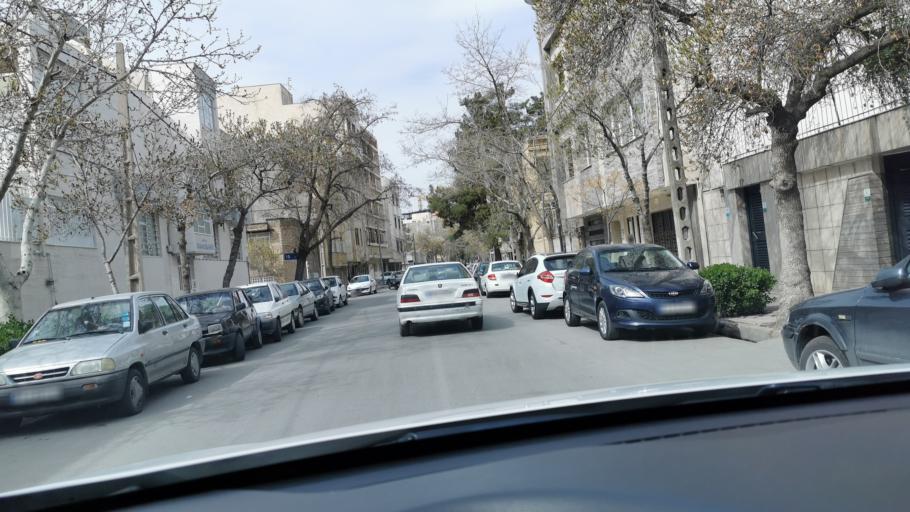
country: IR
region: Razavi Khorasan
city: Mashhad
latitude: 36.2898
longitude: 59.5770
